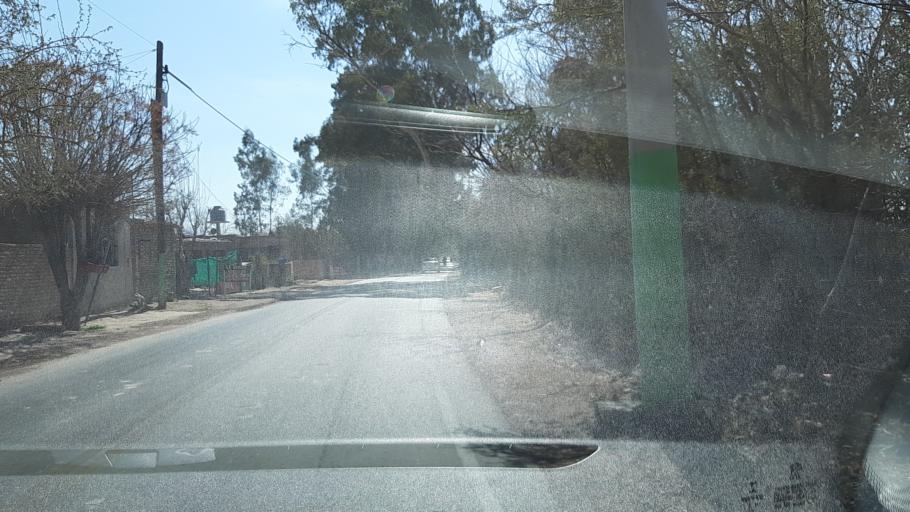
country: AR
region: San Juan
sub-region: Departamento de Rivadavia
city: Rivadavia
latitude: -31.5368
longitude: -68.6173
